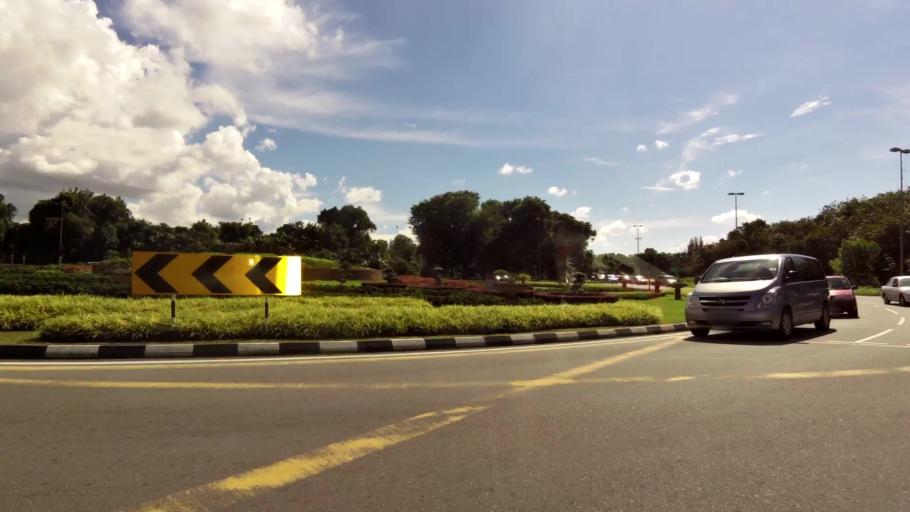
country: BN
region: Brunei and Muara
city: Bandar Seri Begawan
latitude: 4.9425
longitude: 114.9407
